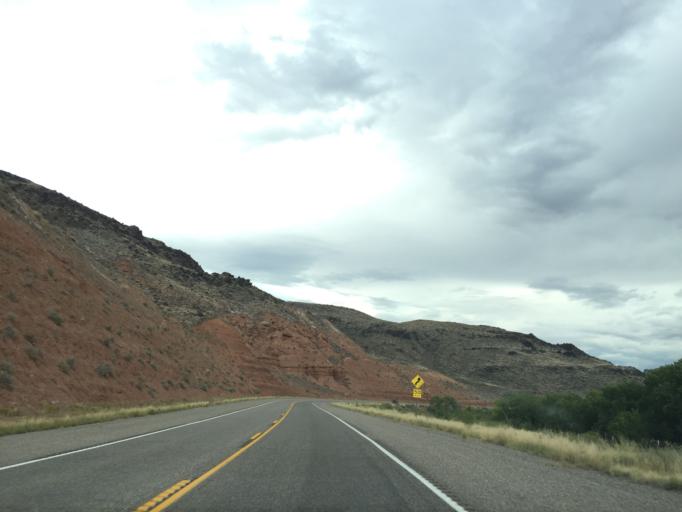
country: US
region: Utah
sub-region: Washington County
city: LaVerkin
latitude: 37.1789
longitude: -113.1205
